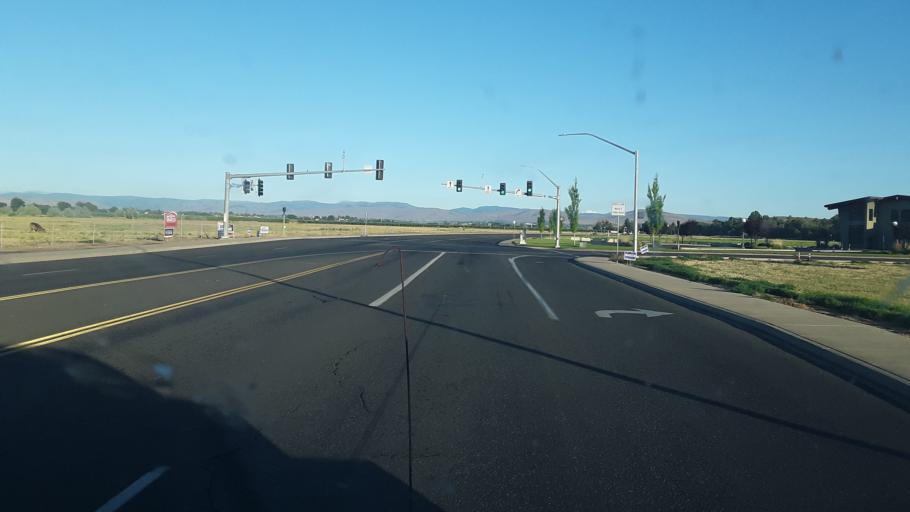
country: US
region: Washington
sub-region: Yakima County
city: West Valley
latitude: 46.5750
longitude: -120.5612
